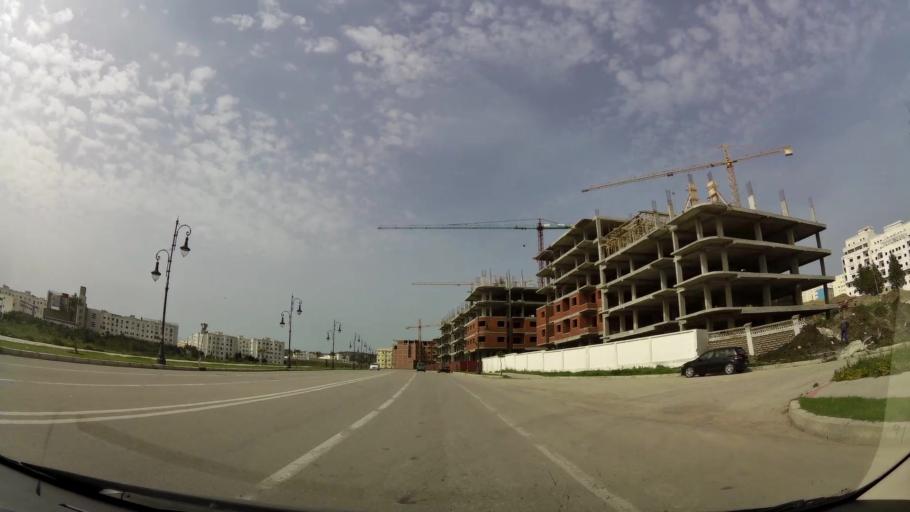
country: MA
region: Tanger-Tetouan
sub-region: Tanger-Assilah
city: Boukhalef
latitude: 35.7329
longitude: -5.8740
